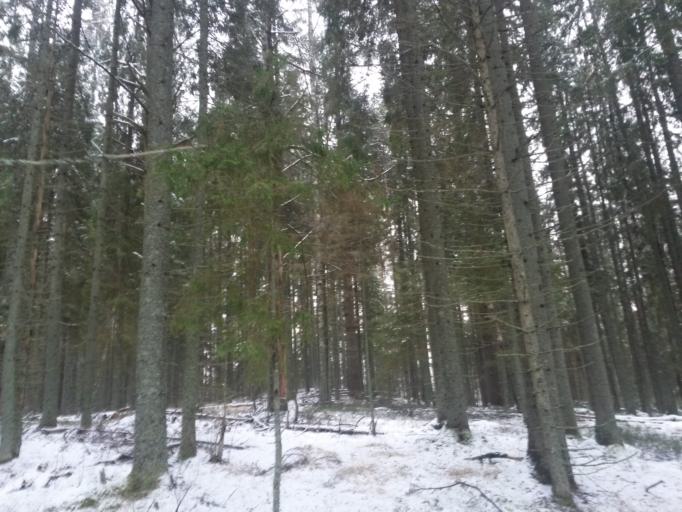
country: RU
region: Novgorod
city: Valday
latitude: 57.9606
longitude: 33.0240
